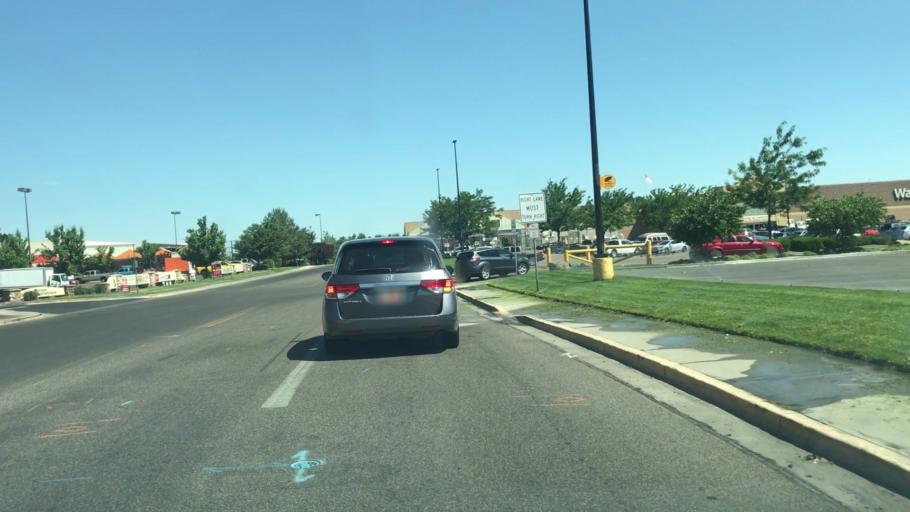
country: US
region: Oregon
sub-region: Malheur County
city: Ontario
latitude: 44.0254
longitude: -116.9403
